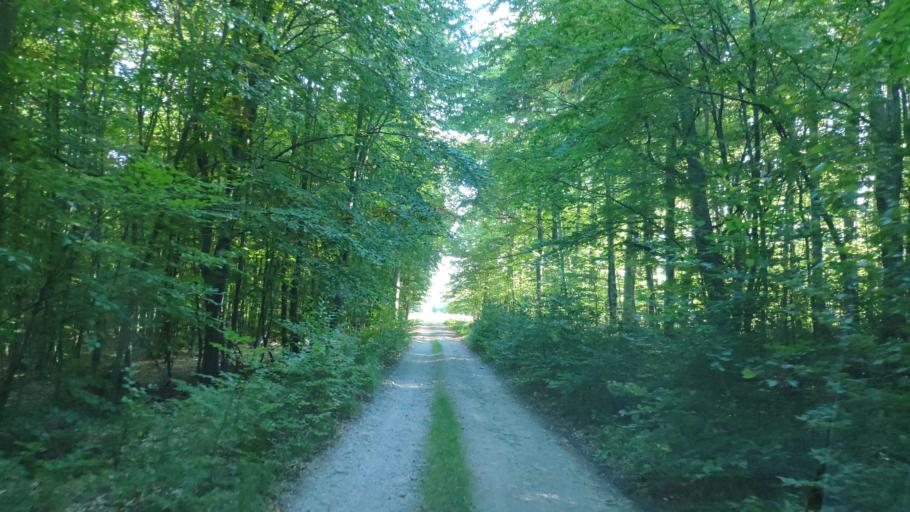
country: SK
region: Presovsky
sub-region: Okres Presov
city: Presov
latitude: 48.8810
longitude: 21.1972
